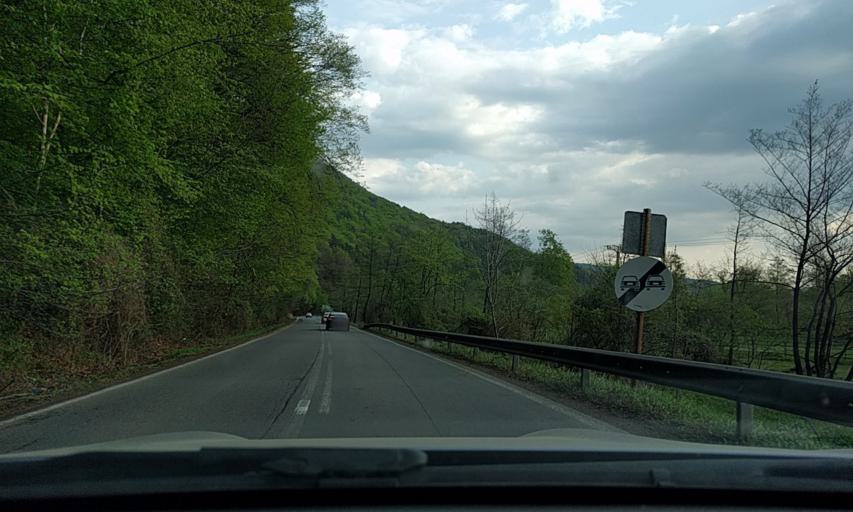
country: RO
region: Bacau
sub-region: Oras Slanic-Moldova
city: Slanic-Moldova
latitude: 46.1564
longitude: 26.4607
